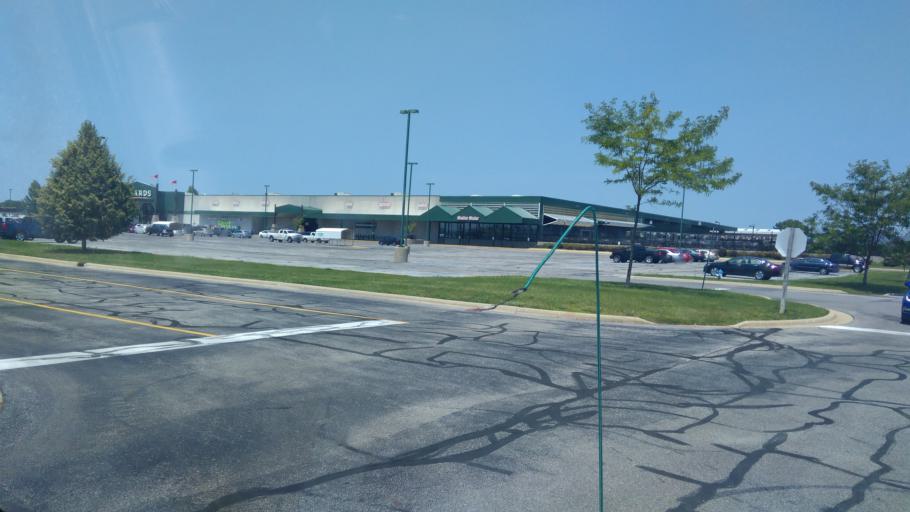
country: US
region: Ohio
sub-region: Marion County
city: Marion
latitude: 40.5825
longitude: -83.0646
